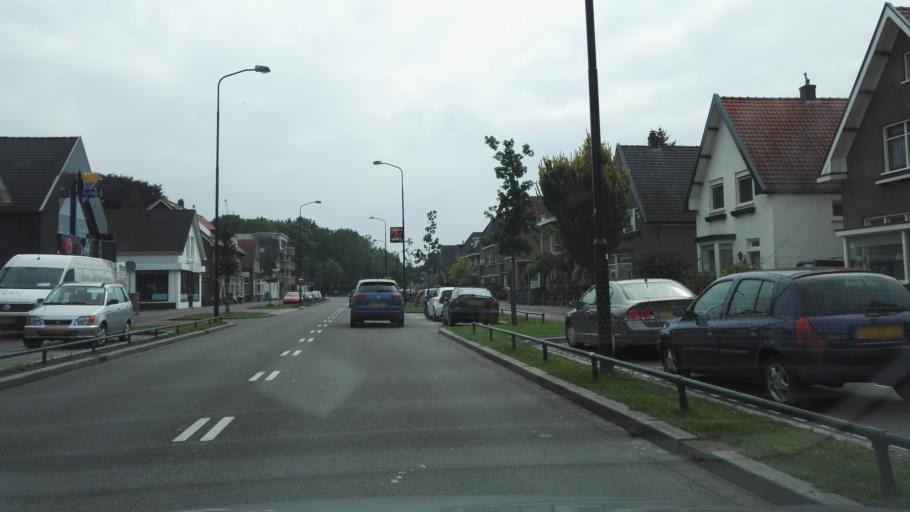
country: NL
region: Gelderland
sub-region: Gemeente Apeldoorn
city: Apeldoorn
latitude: 52.1987
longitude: 5.9599
